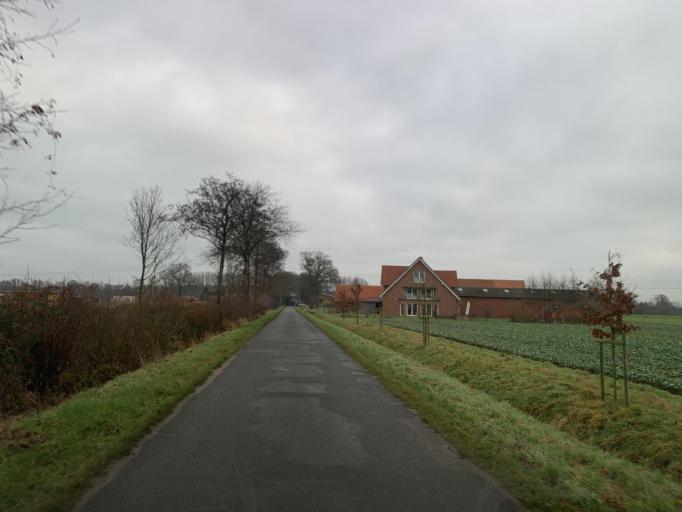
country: DE
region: North Rhine-Westphalia
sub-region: Regierungsbezirk Munster
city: Greven
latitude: 52.0597
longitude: 7.5753
